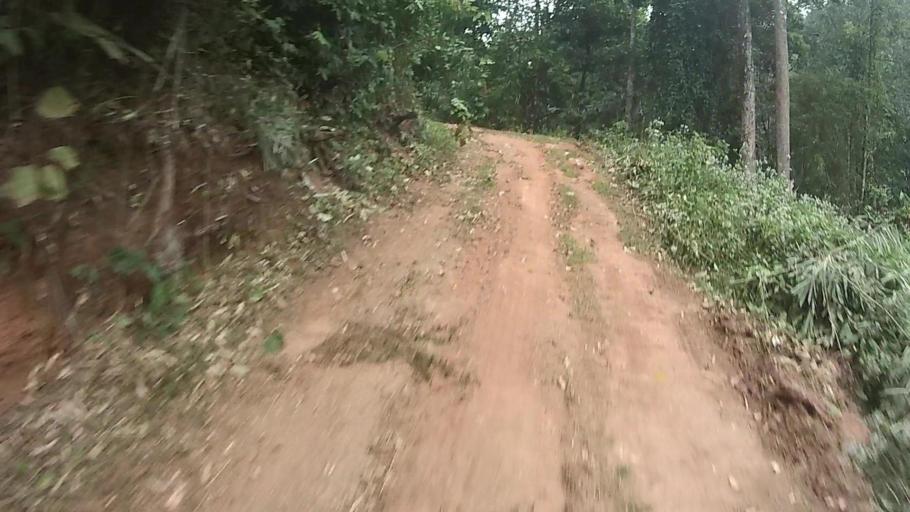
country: TH
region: Chiang Mai
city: Mae On
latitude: 18.7918
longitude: 99.3415
